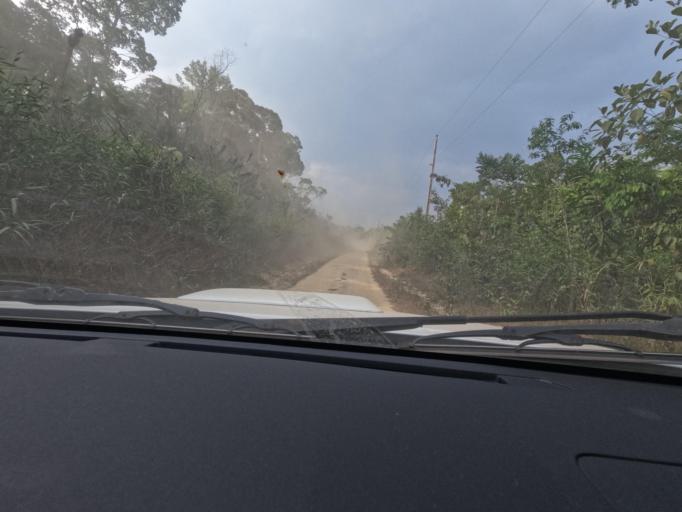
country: BR
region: Rondonia
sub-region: Porto Velho
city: Porto Velho
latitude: -8.5670
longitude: -64.0225
